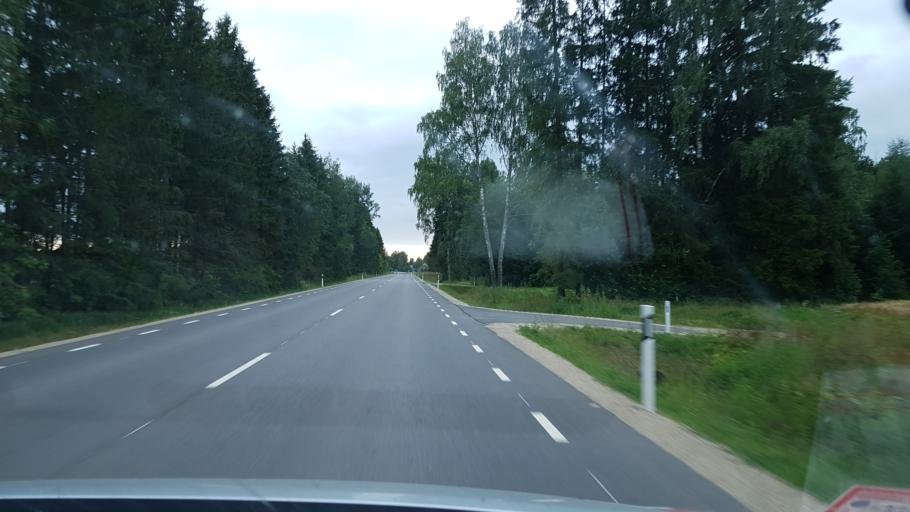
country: EE
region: Polvamaa
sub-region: Polva linn
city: Polva
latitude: 57.9487
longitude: 27.2310
